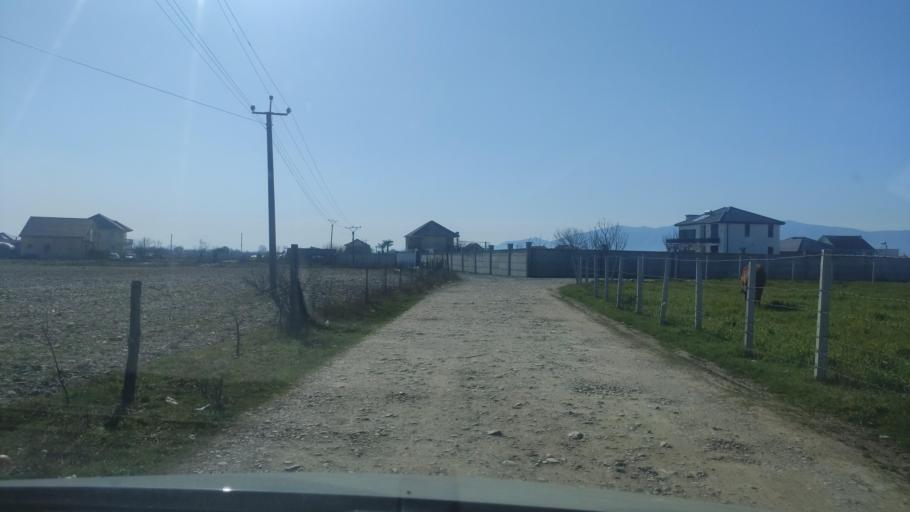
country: AL
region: Shkoder
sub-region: Rrethi i Malesia e Madhe
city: Grude-Fushe
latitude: 42.1602
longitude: 19.4582
